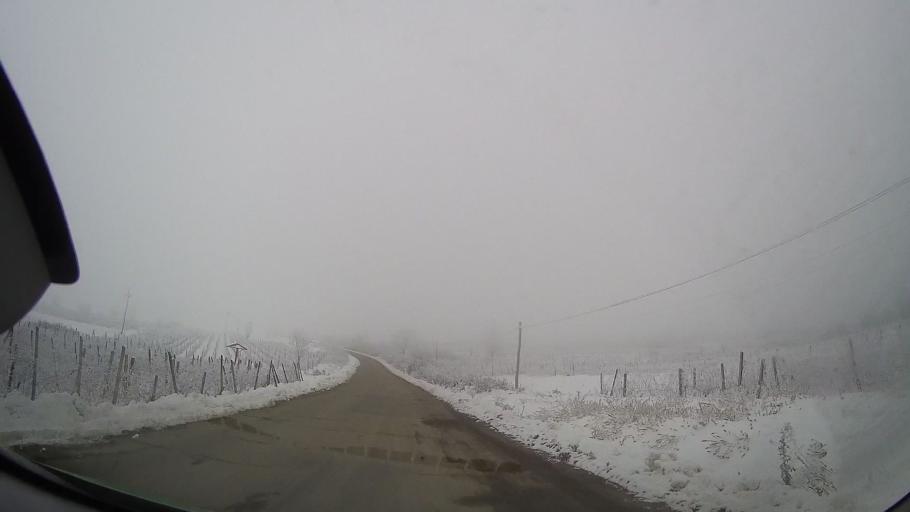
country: RO
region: Iasi
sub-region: Comuna Tibanesti
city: Tibanesti
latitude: 46.8935
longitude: 27.3068
